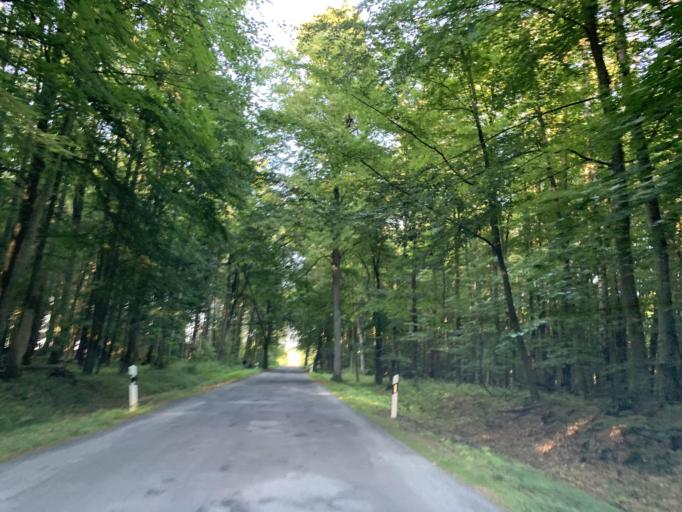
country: DE
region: Mecklenburg-Vorpommern
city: Carpin
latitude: 53.3456
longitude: 13.2422
